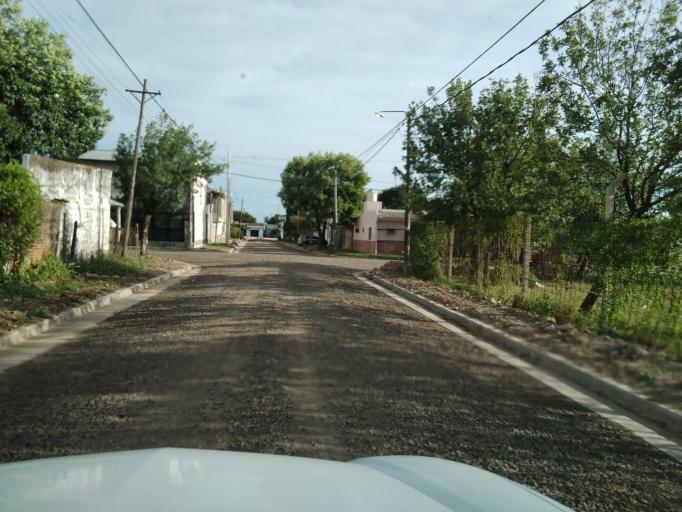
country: AR
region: Corrientes
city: Corrientes
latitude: -27.4900
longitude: -58.8466
